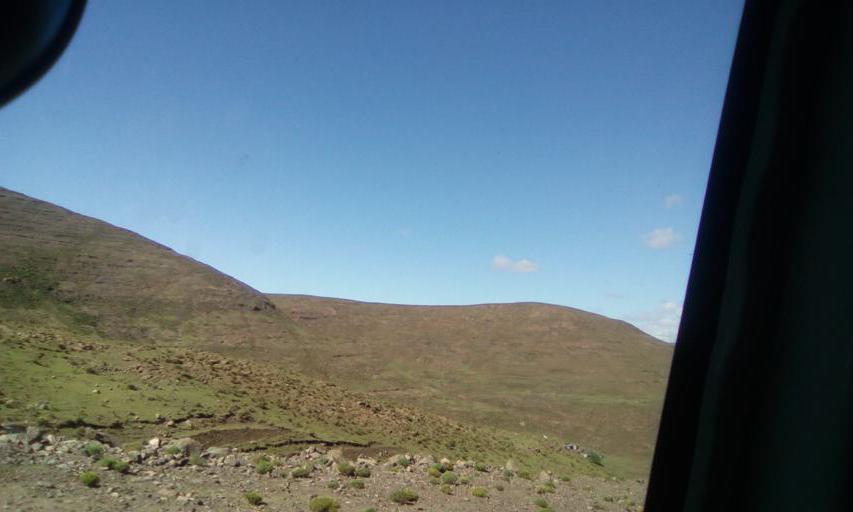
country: LS
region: Maseru
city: Nako
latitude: -29.8890
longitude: 28.1124
